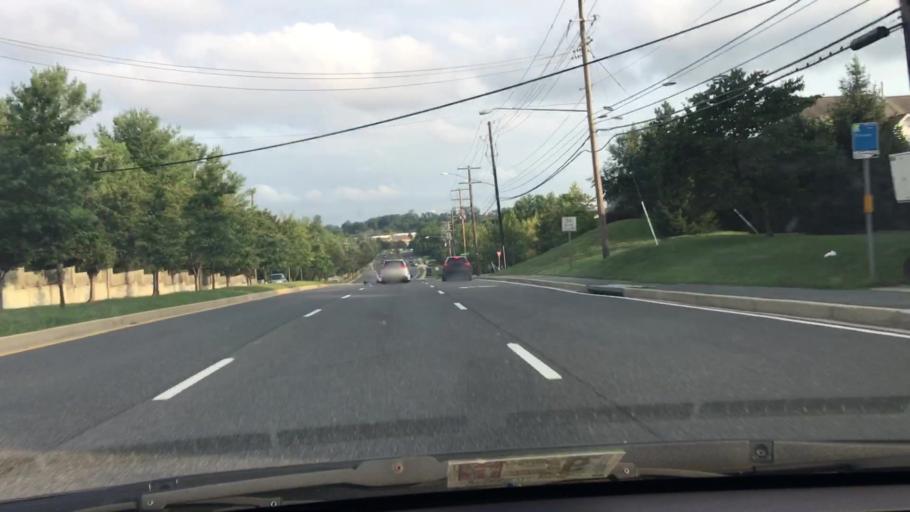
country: US
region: Maryland
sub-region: Montgomery County
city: Germantown
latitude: 39.1876
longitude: -77.2406
